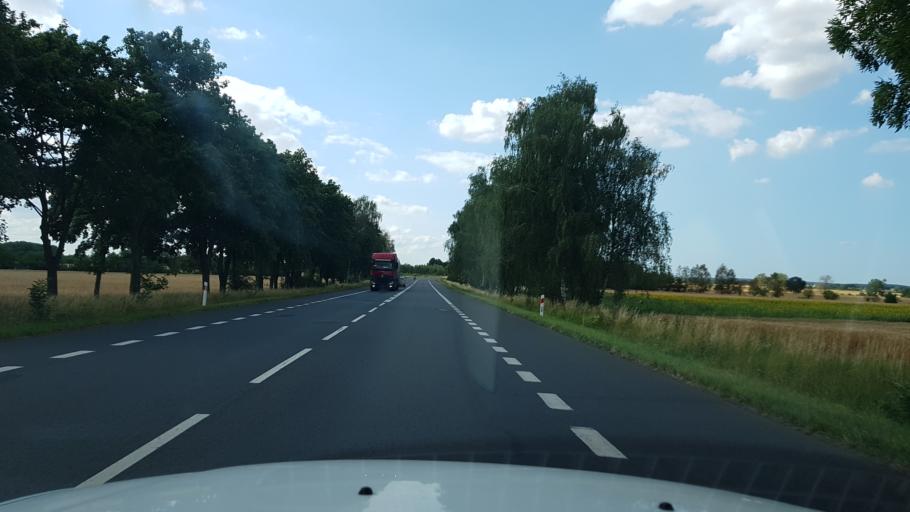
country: PL
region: West Pomeranian Voivodeship
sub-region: Powiat gryfinski
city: Stare Czarnowo
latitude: 53.2139
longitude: 14.8028
